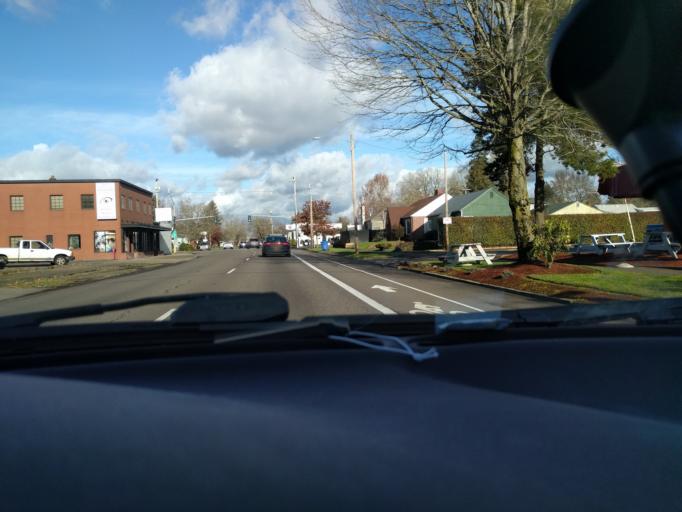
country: US
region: Oregon
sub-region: Marion County
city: Salem
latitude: 44.9508
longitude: -123.0224
